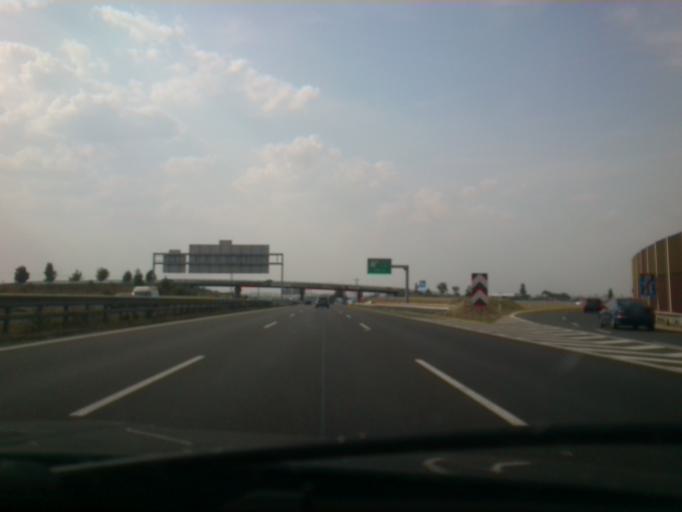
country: CZ
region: Central Bohemia
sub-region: Okres Praha-Zapad
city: Pruhonice
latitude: 49.9925
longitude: 14.5891
